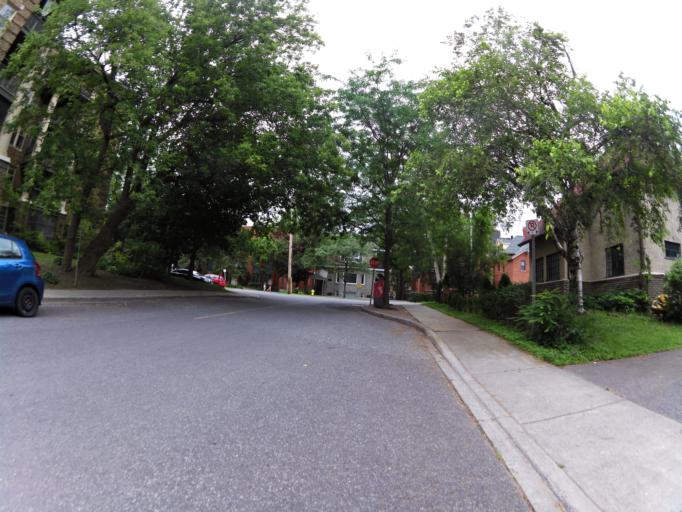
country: CA
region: Ontario
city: Ottawa
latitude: 45.4282
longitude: -75.6751
